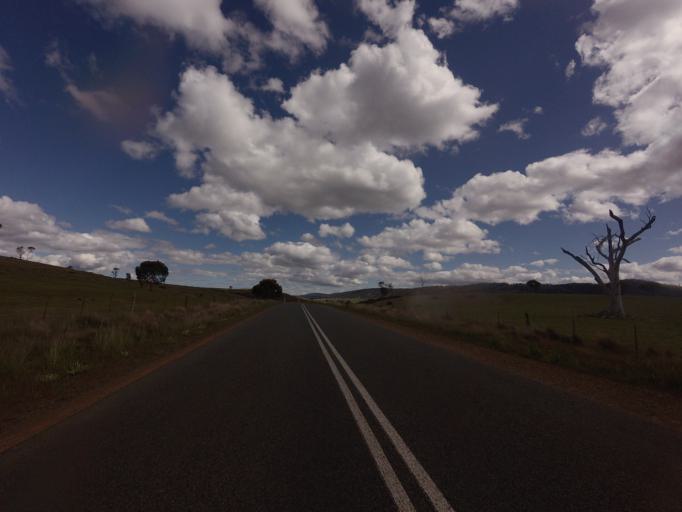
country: AU
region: Tasmania
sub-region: Brighton
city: Bridgewater
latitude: -42.3955
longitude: 147.3148
